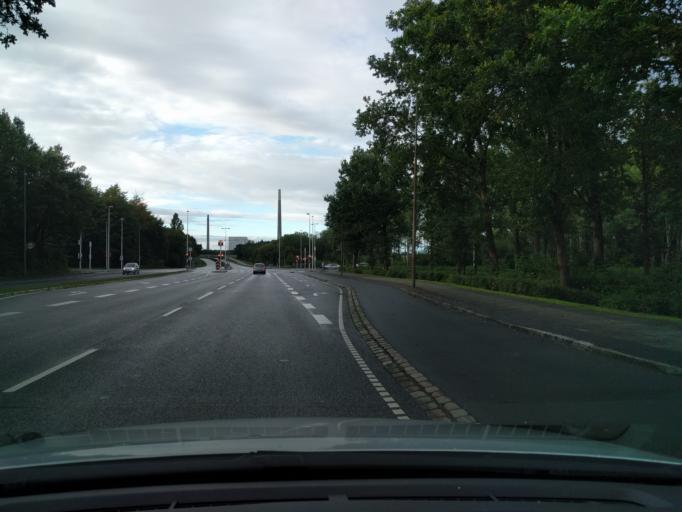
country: DK
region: South Denmark
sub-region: Odense Kommune
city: Seden
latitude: 55.4158
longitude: 10.4214
